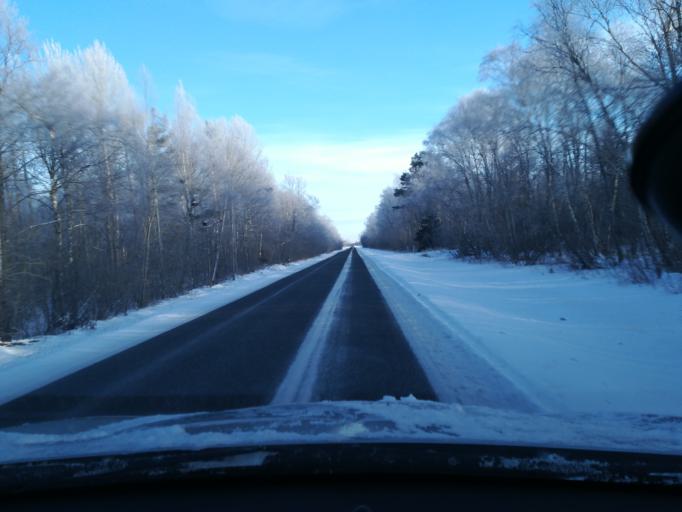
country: EE
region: Harju
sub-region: Keila linn
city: Keila
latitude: 59.3961
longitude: 24.3329
